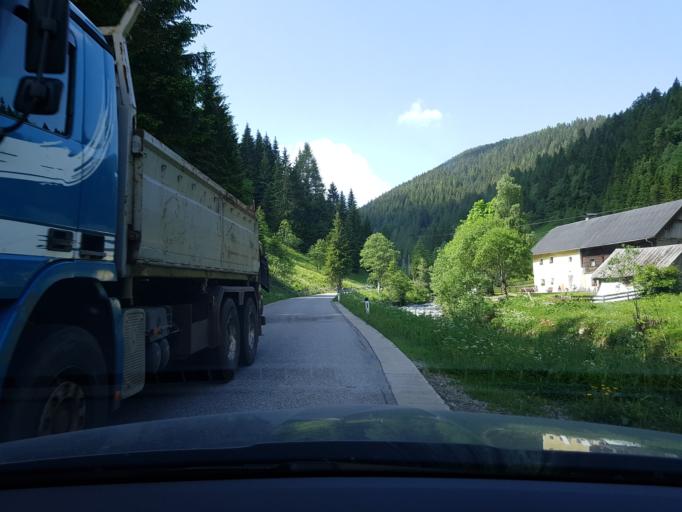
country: AT
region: Salzburg
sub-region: Politischer Bezirk Tamsweg
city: Thomatal
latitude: 47.0528
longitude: 13.7136
